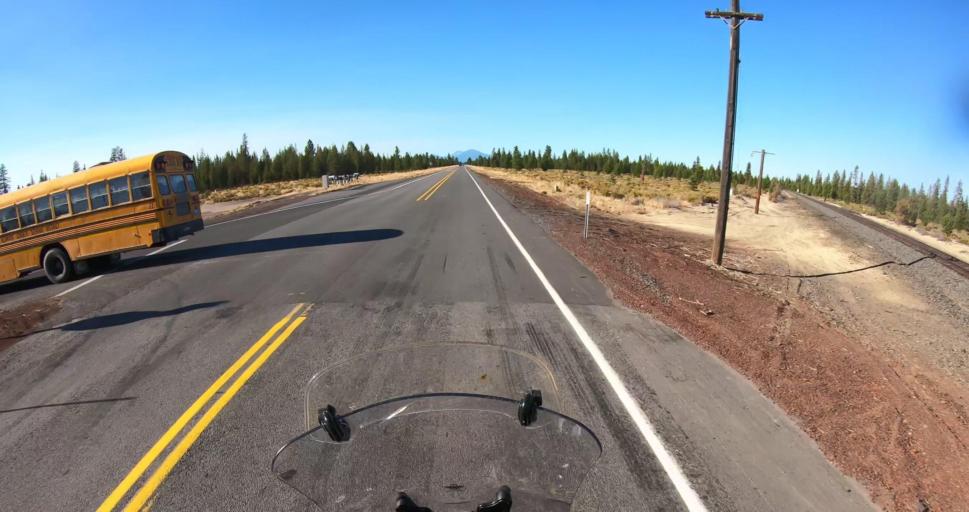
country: US
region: Oregon
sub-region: Deschutes County
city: La Pine
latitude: 43.6076
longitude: -121.5015
